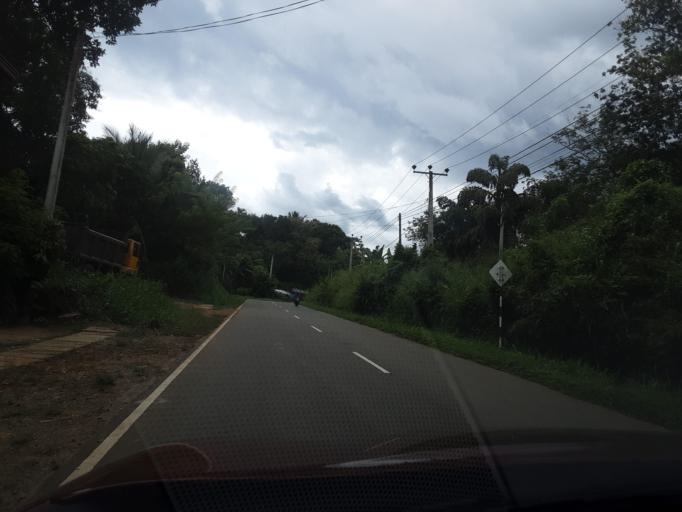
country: LK
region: Uva
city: Monaragala
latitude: 6.9055
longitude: 81.2203
